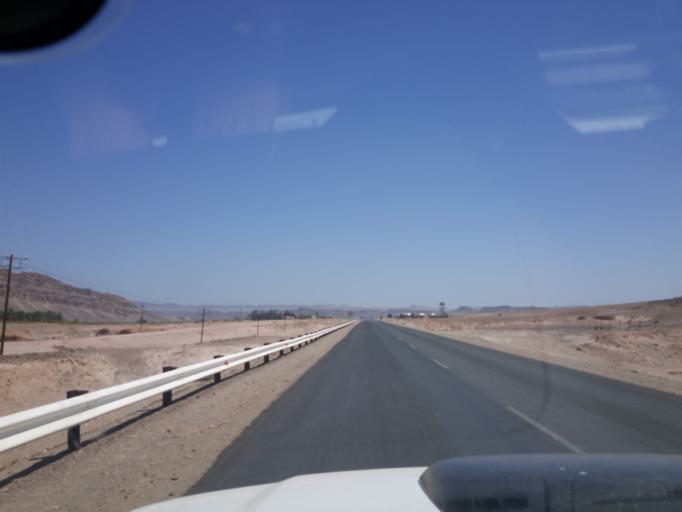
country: ZA
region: Northern Cape
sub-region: Namakwa District Municipality
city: Port Nolloth
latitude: -28.7526
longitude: 17.6193
